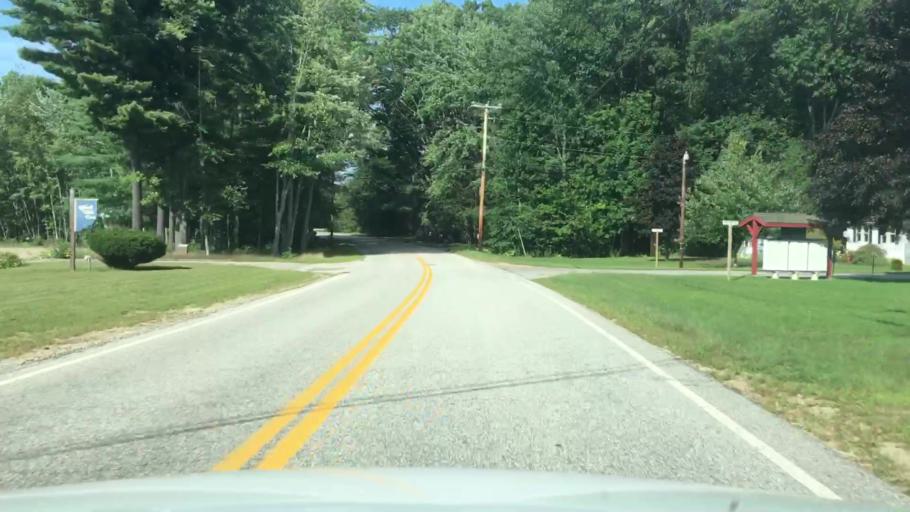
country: US
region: New Hampshire
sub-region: Belknap County
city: Gilford
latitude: 43.5694
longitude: -71.4070
